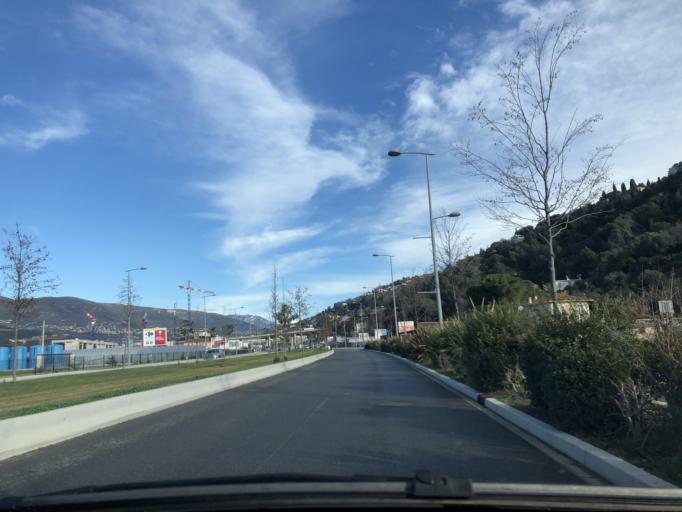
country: FR
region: Provence-Alpes-Cote d'Azur
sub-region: Departement des Alpes-Maritimes
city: Saint-Laurent-du-Var
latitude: 43.7018
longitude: 7.1971
